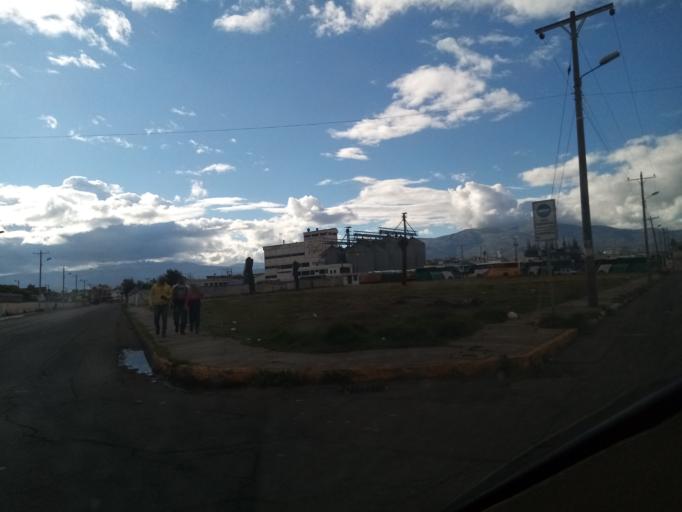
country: EC
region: Chimborazo
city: Riobamba
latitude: -1.6858
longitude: -78.6319
